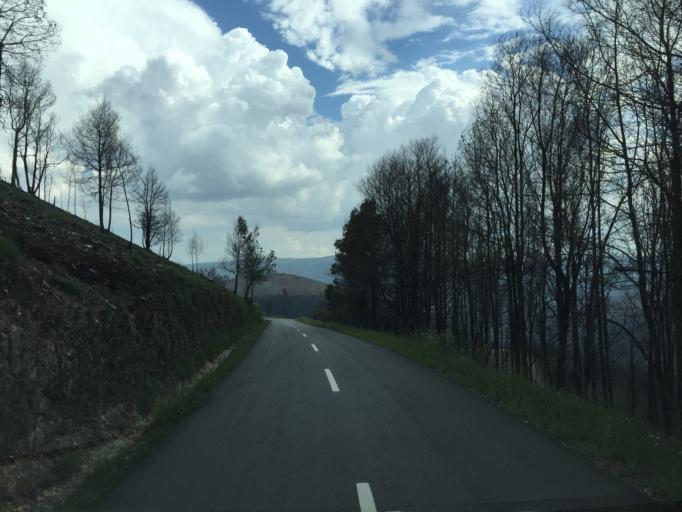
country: PT
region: Coimbra
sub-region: Arganil
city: Arganil
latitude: 40.1777
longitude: -7.9751
